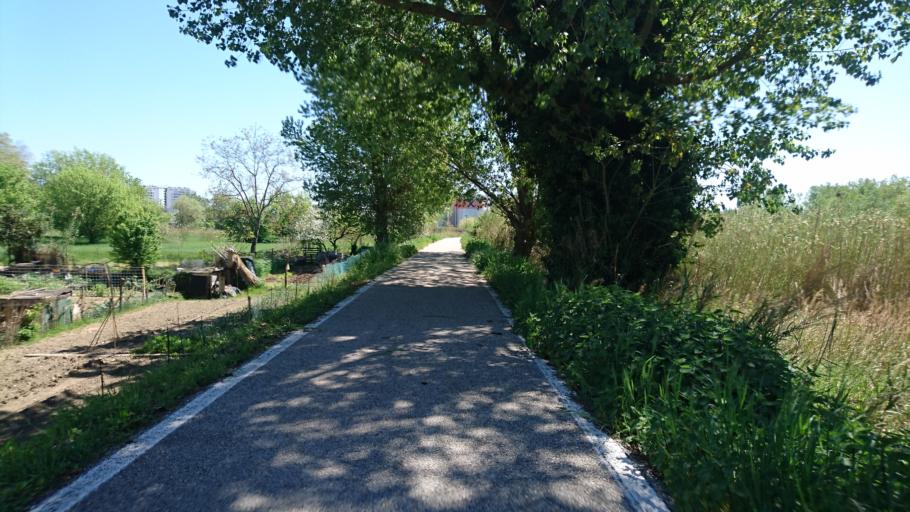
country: IT
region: The Marches
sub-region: Provincia di Pesaro e Urbino
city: Pesaro
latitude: 43.9068
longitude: 12.8815
